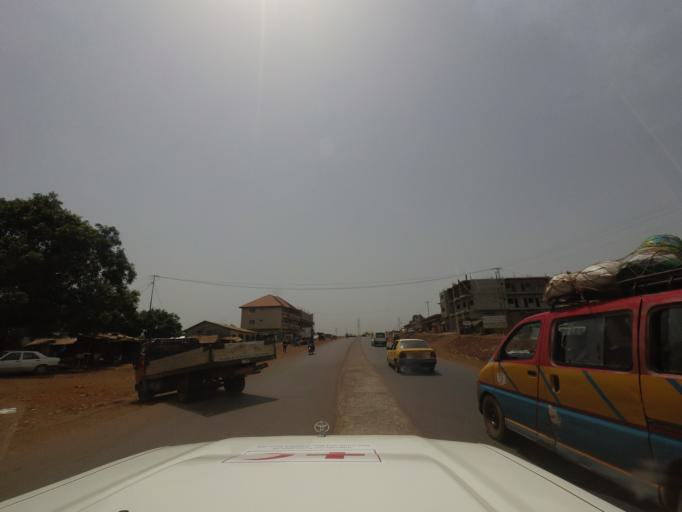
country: GN
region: Kindia
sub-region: Prefecture de Dubreka
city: Dubreka
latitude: 9.7209
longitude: -13.4743
